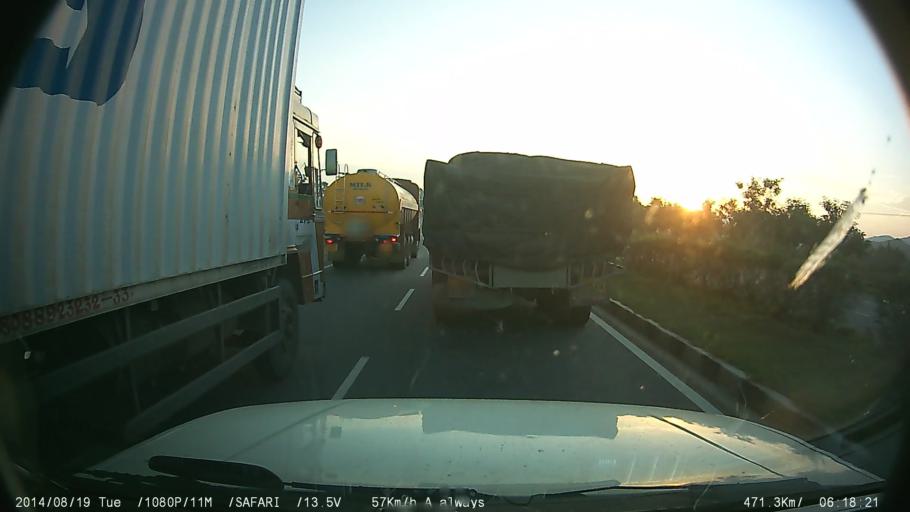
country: IN
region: Tamil Nadu
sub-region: Dharmapuri
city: Dharmapuri
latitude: 12.0016
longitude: 78.0770
